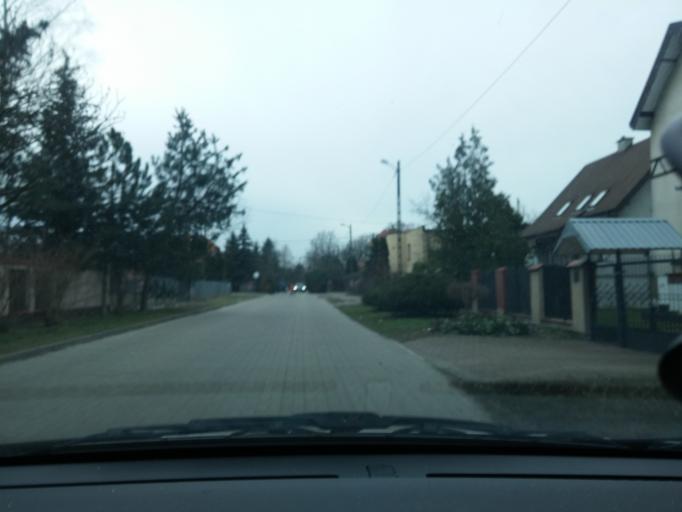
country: PL
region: Masovian Voivodeship
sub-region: Warszawa
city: Wawer
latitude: 52.2124
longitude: 21.1475
